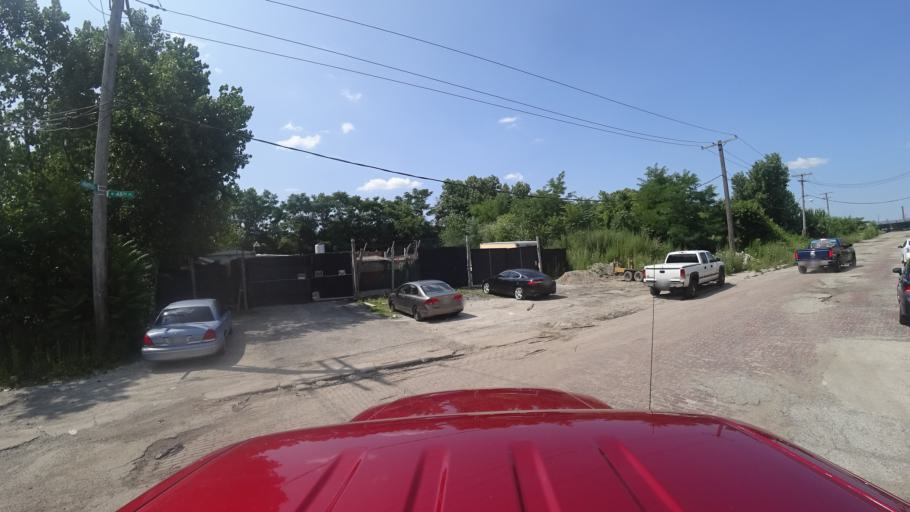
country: US
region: Illinois
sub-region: Cook County
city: Cicero
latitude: 41.8053
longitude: -87.7003
